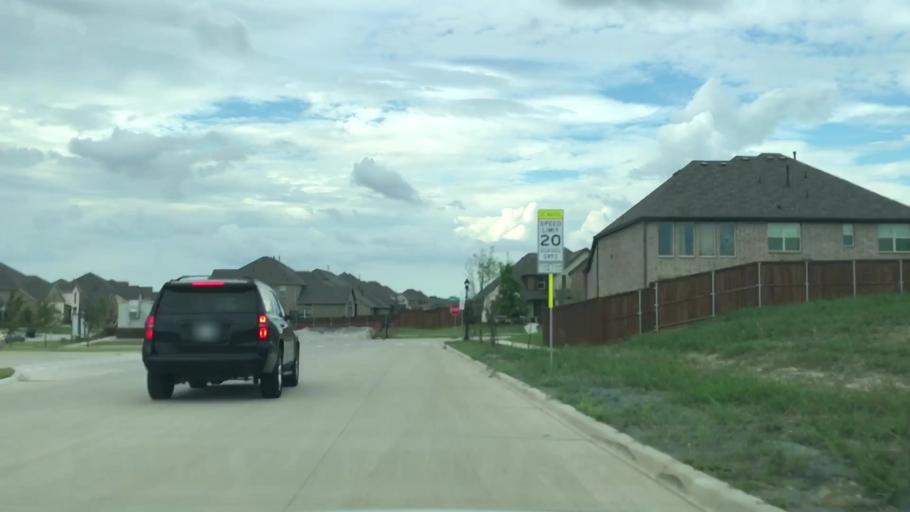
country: US
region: Texas
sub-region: Collin County
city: Prosper
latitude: 33.1901
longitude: -96.7785
